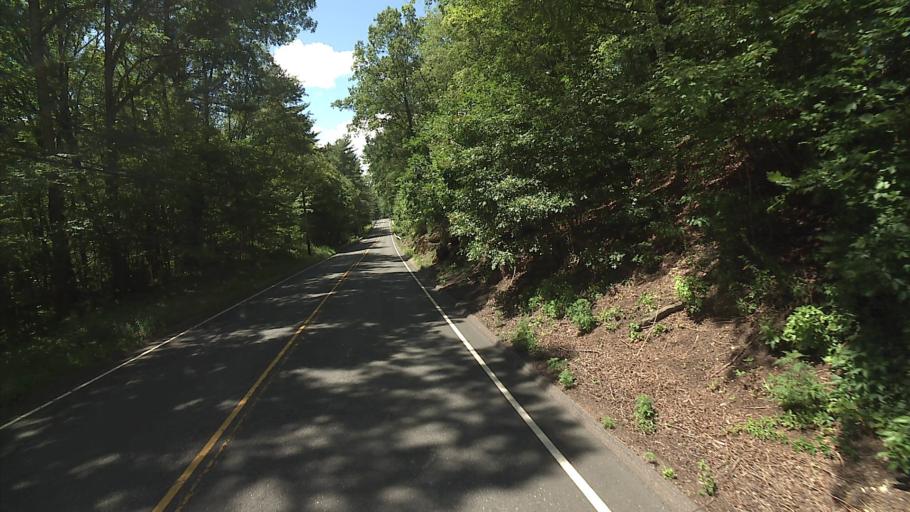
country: US
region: Connecticut
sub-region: Litchfield County
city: New Hartford Center
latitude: 41.9233
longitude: -72.9316
